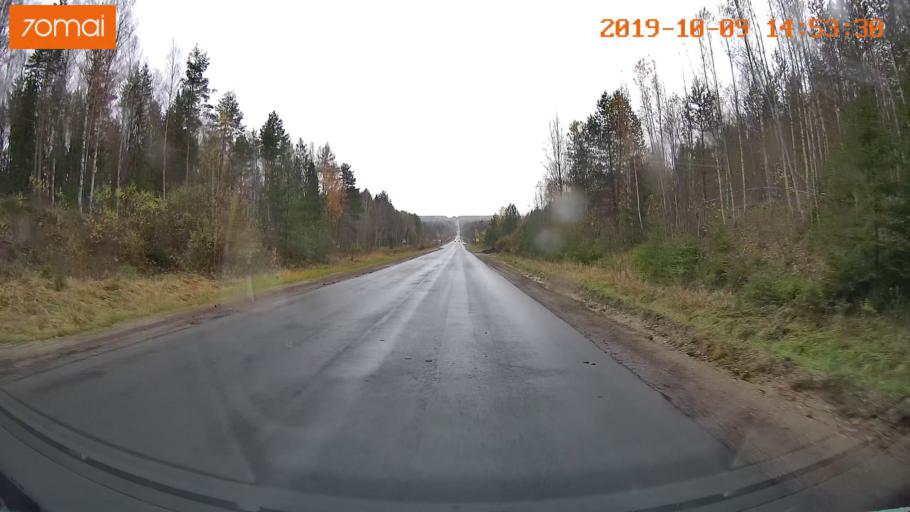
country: RU
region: Kostroma
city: Chistyye Bory
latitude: 58.3668
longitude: 41.6387
